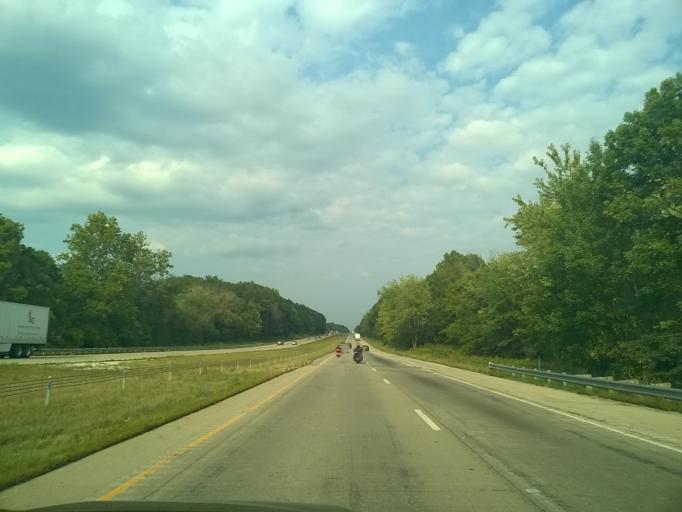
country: US
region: Indiana
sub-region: Clay County
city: Brazil
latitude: 39.4914
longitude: -86.9893
